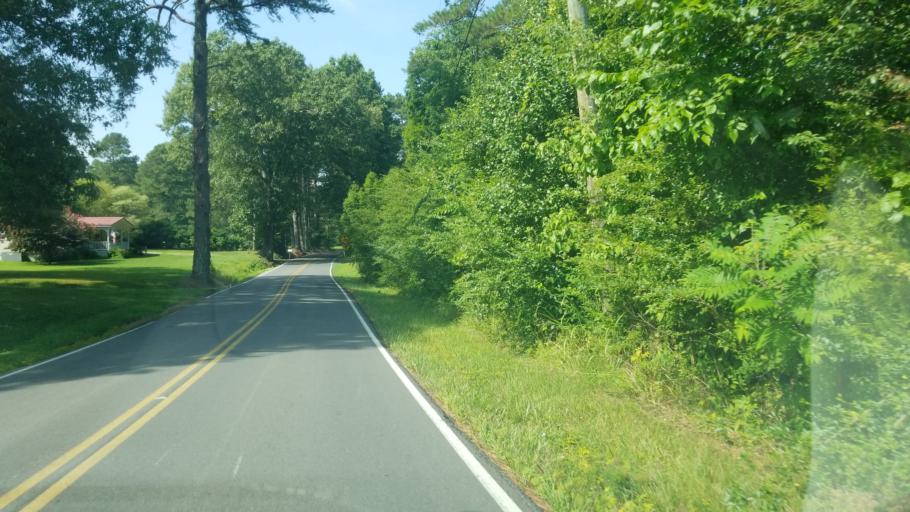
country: US
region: Tennessee
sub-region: Hamilton County
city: Collegedale
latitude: 35.0787
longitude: -84.9971
